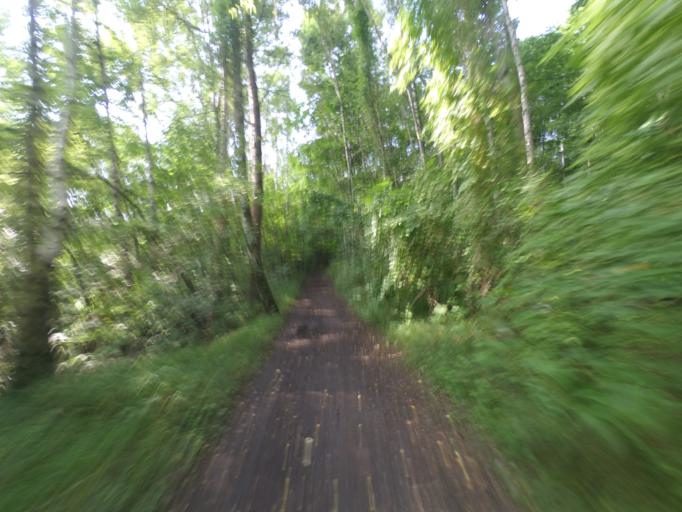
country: DE
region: Schleswig-Holstein
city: Glinde
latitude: 53.5045
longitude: 10.1768
